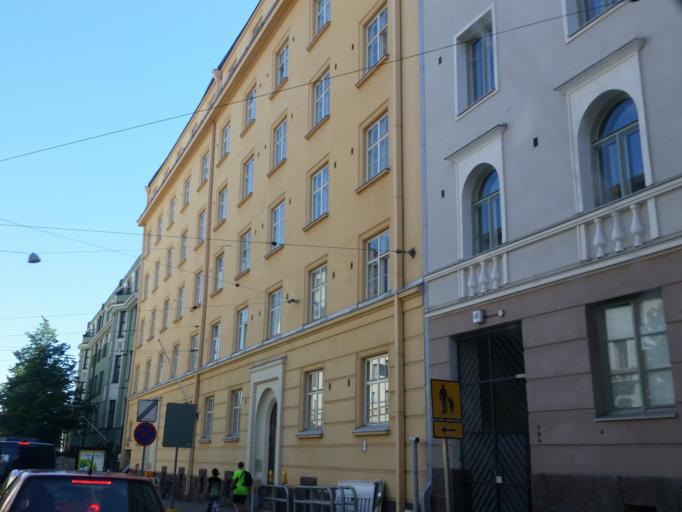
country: FI
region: Uusimaa
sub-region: Helsinki
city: Helsinki
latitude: 60.1810
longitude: 24.9257
